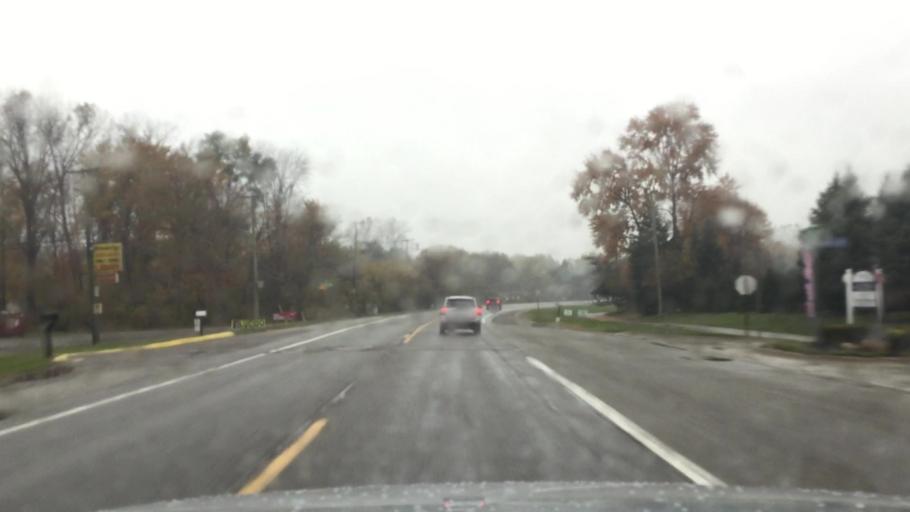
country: US
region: Michigan
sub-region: Macomb County
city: New Baltimore
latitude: 42.6600
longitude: -82.7710
